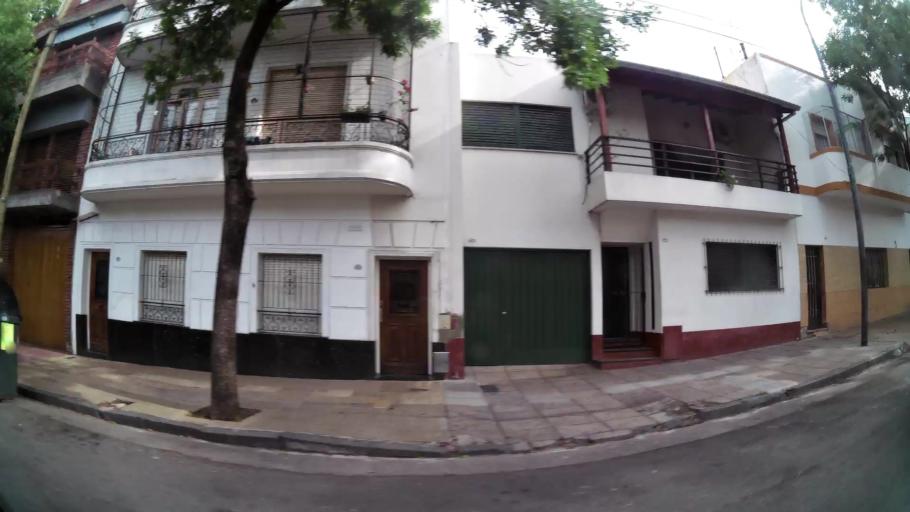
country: AR
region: Buenos Aires F.D.
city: Buenos Aires
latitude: -34.6280
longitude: -58.4164
